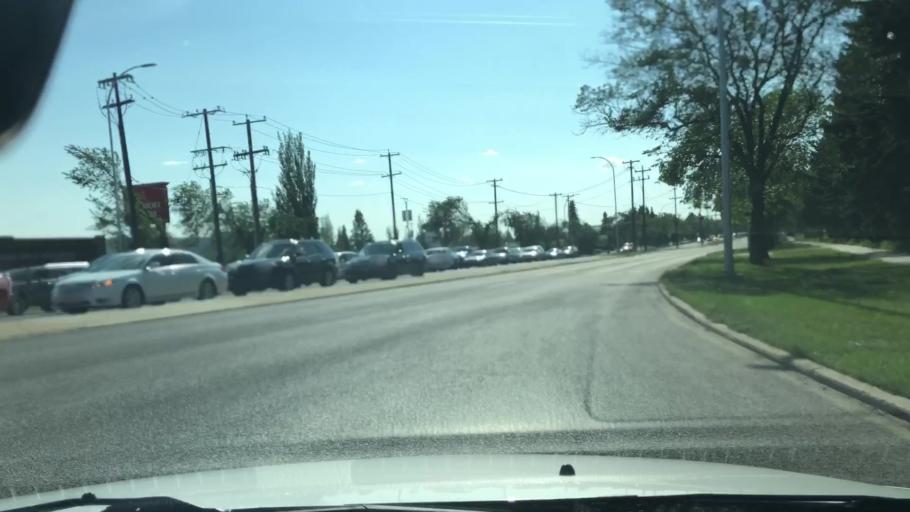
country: CA
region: Alberta
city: Edmonton
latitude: 53.5996
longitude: -113.4927
